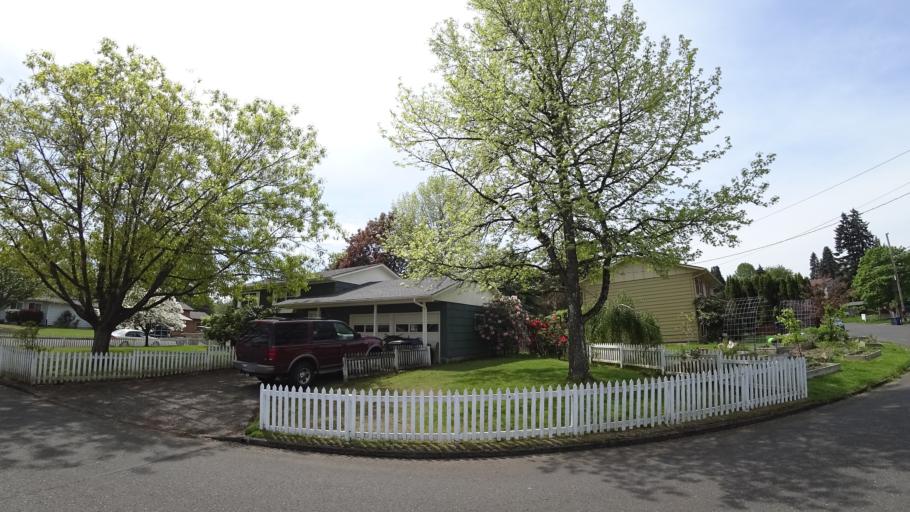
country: US
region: Oregon
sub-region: Clackamas County
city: Milwaukie
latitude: 45.4560
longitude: -122.6101
